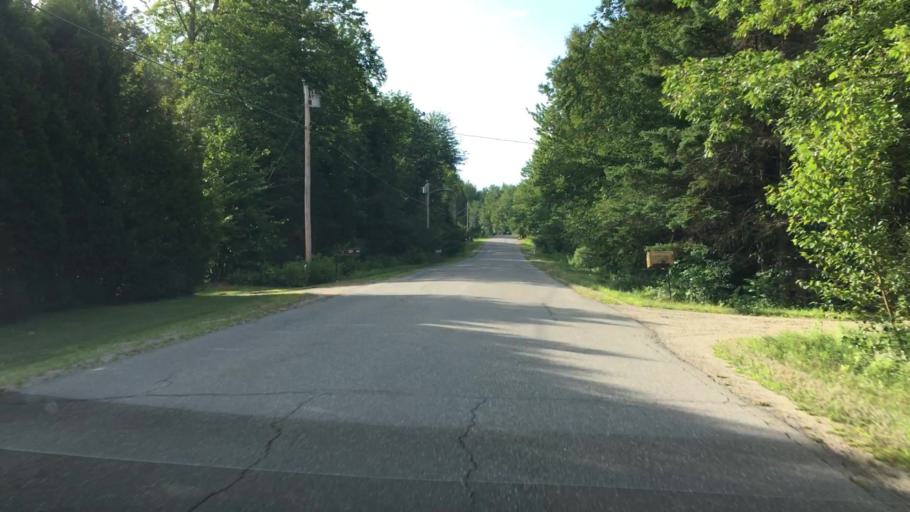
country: US
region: Maine
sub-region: Waldo County
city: Stockton Springs
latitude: 44.4903
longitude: -68.8667
